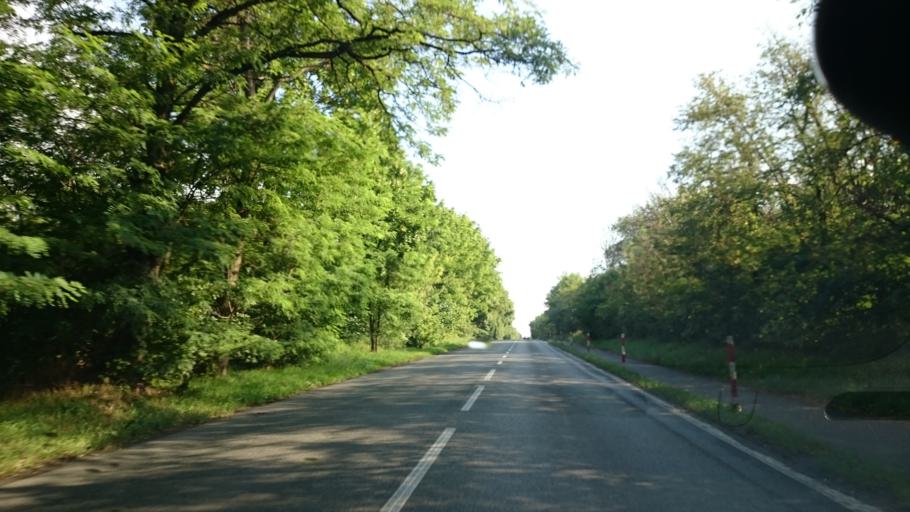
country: PL
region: Opole Voivodeship
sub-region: Powiat opolski
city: Opole
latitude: 50.6851
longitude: 17.9262
